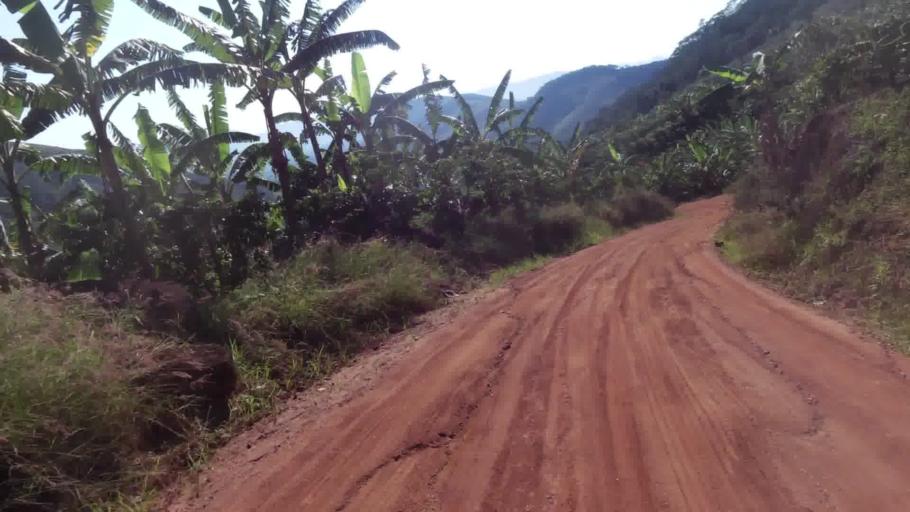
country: BR
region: Espirito Santo
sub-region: Alfredo Chaves
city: Alfredo Chaves
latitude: -20.6957
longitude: -40.7844
